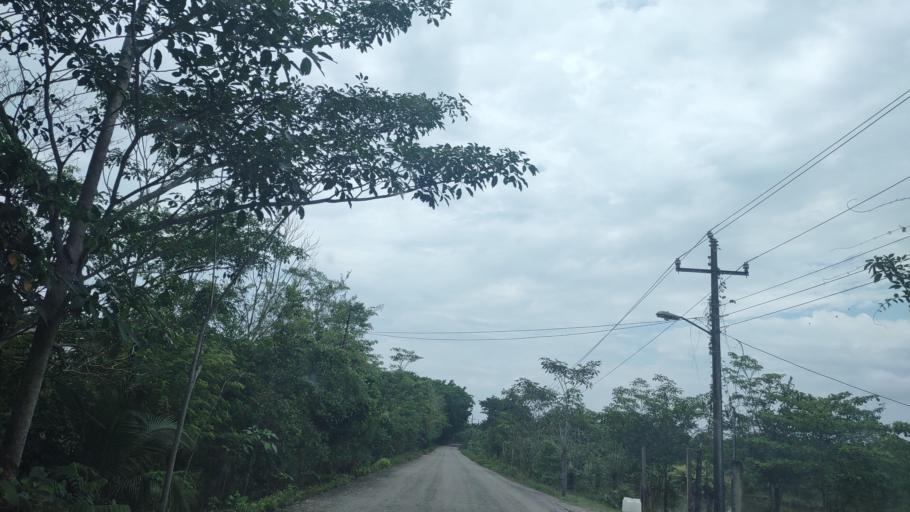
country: MX
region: Tabasco
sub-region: Huimanguillo
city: Francisco Rueda
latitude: 17.5333
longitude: -94.1275
